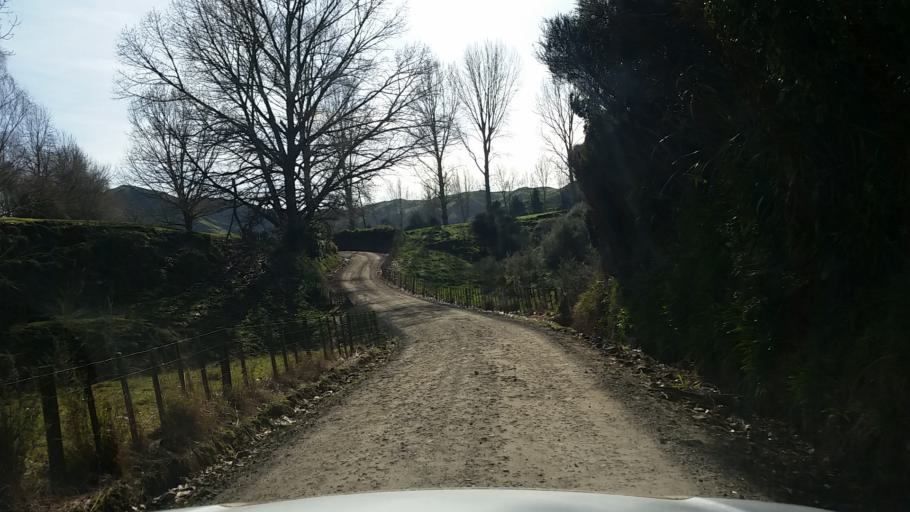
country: NZ
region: Taranaki
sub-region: South Taranaki District
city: Eltham
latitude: -39.3517
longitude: 174.5131
